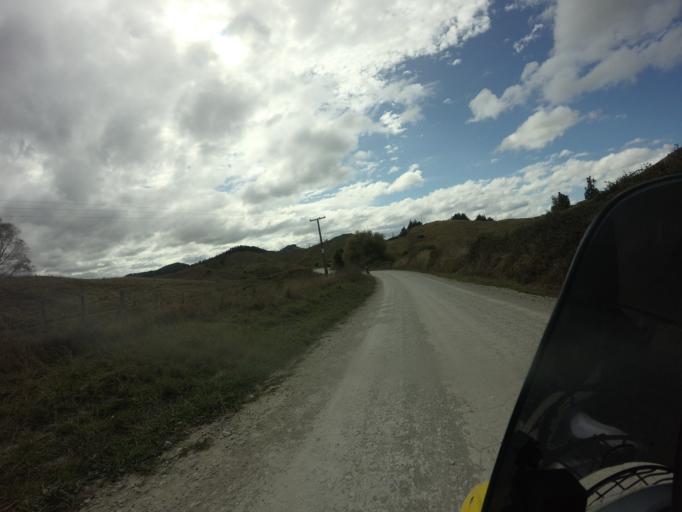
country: NZ
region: Gisborne
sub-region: Gisborne District
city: Gisborne
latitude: -38.6972
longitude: 177.7282
